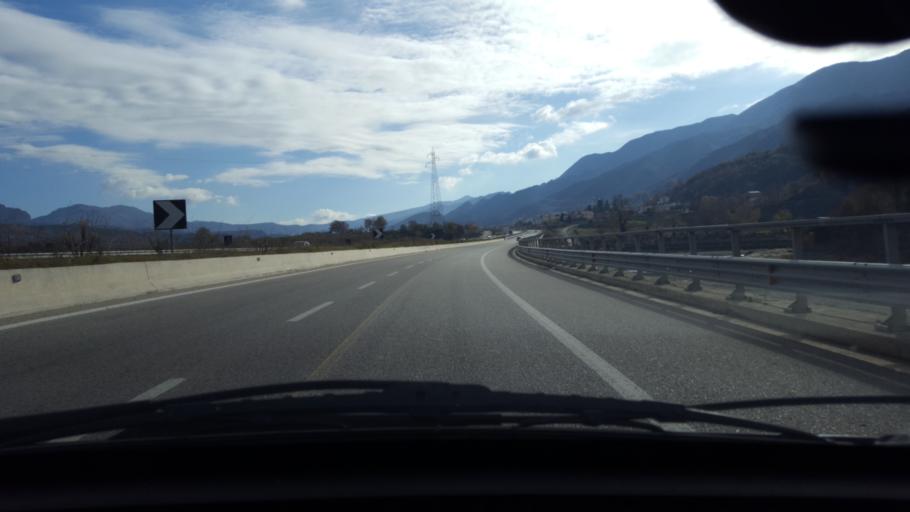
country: AL
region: Tirane
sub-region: Rrethi i Tiranes
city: Berzhite
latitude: 41.2583
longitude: 19.8899
